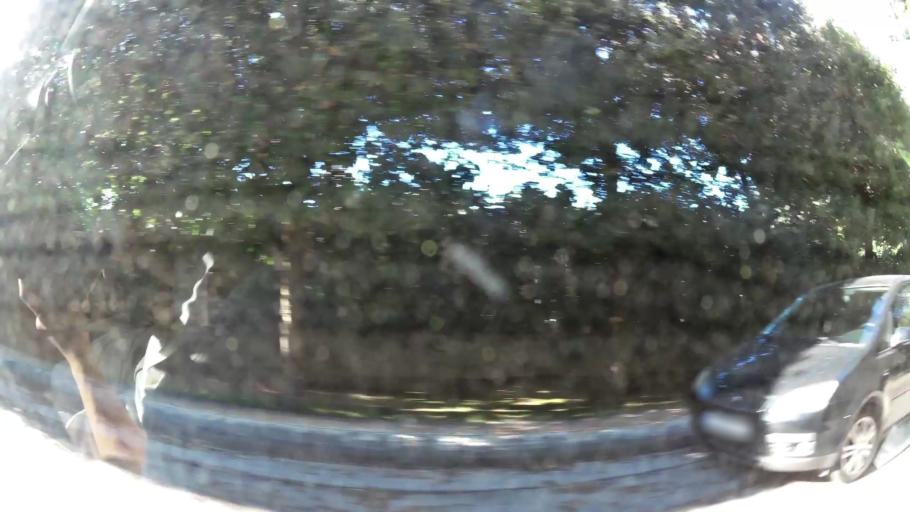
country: GR
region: Attica
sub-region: Nomarchia Athinas
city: Ekali
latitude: 38.1071
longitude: 23.8459
